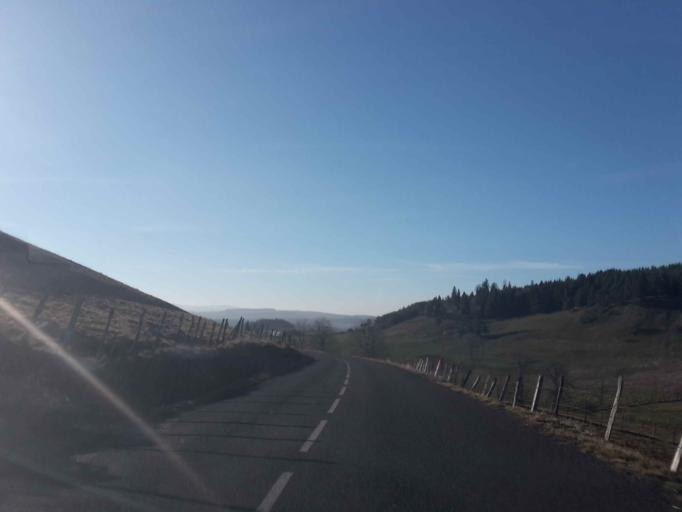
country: FR
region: Auvergne
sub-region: Departement du Cantal
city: Allanche
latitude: 45.2468
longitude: 2.9579
